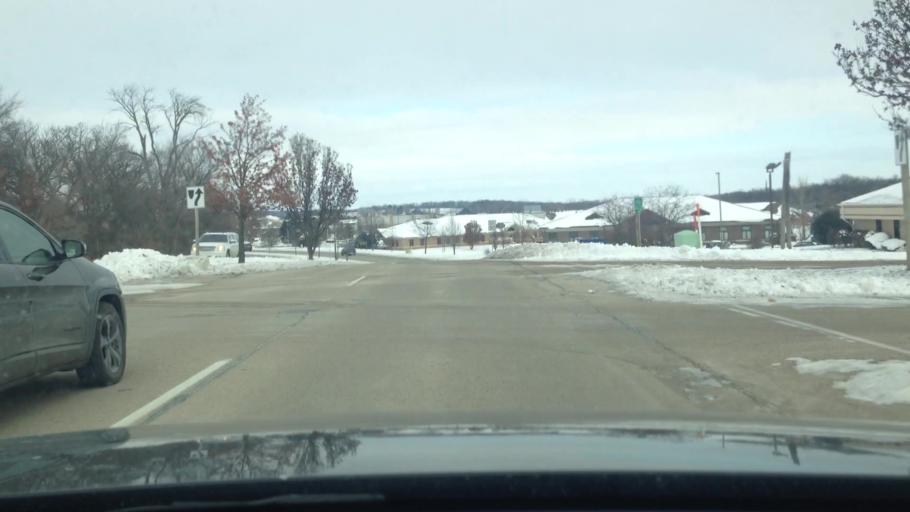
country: US
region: Wisconsin
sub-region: Walworth County
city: Lake Geneva
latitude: 42.5853
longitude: -88.4117
